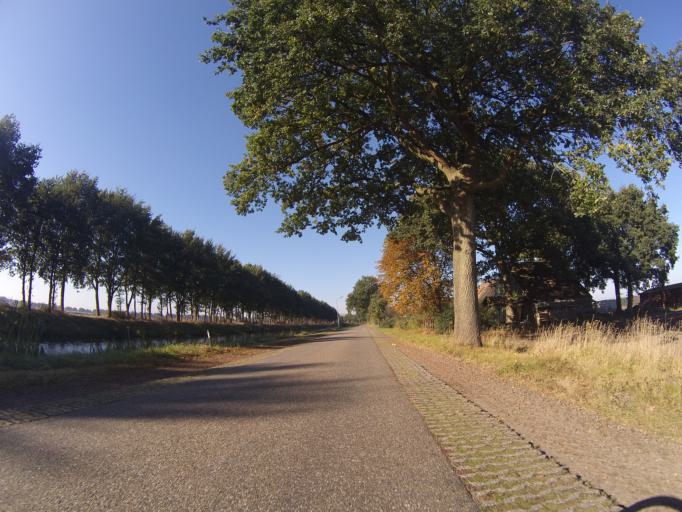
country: NL
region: Drenthe
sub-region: Gemeente Coevorden
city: Dalen
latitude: 52.7424
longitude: 6.7627
